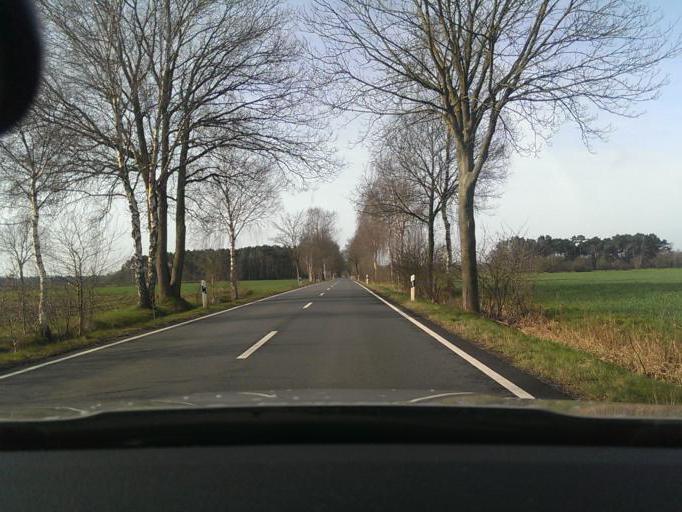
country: DE
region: Lower Saxony
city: Lindwedel
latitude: 52.5406
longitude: 9.6225
